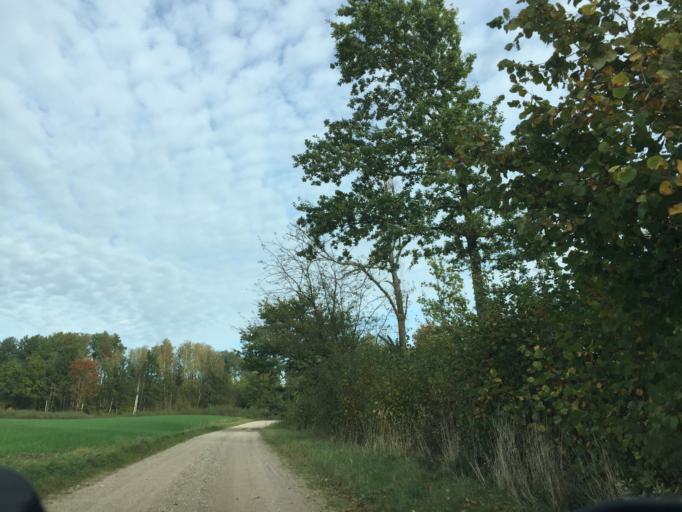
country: LV
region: Jaunpils
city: Jaunpils
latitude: 56.6358
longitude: 23.0716
